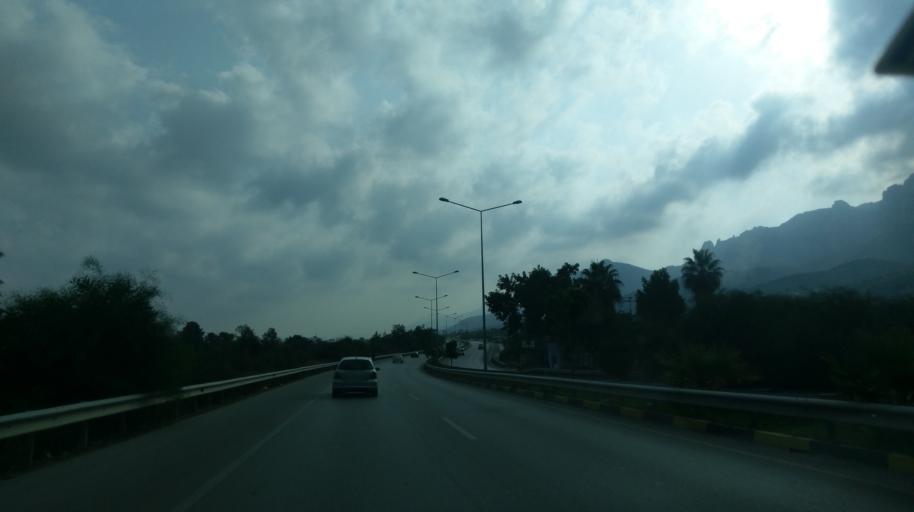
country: CY
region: Keryneia
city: Kyrenia
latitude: 35.3341
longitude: 33.2654
